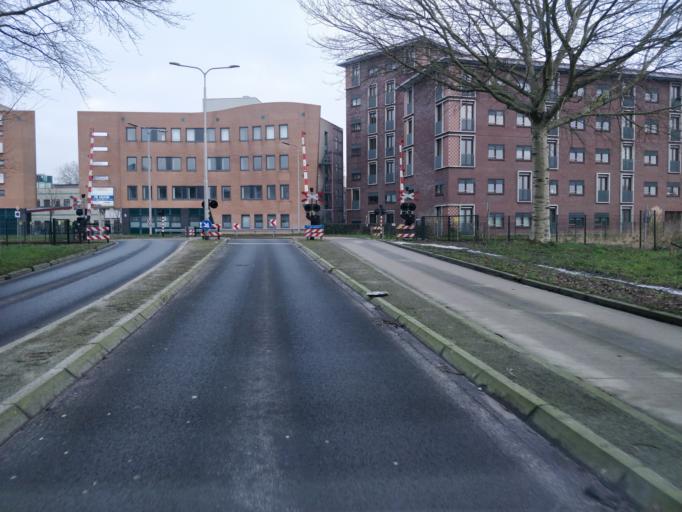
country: NL
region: Friesland
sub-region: Gemeente Leeuwarden
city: Leeuwarden
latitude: 53.1970
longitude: 5.8027
